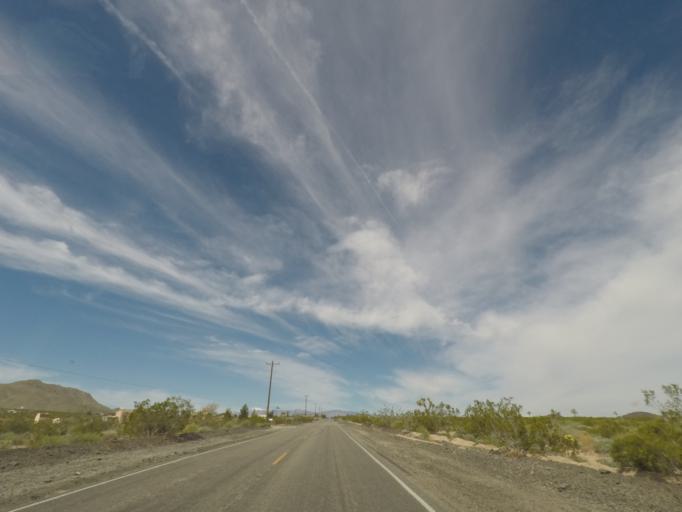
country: US
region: California
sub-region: San Bernardino County
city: Joshua Tree
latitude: 34.1932
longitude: -116.3074
